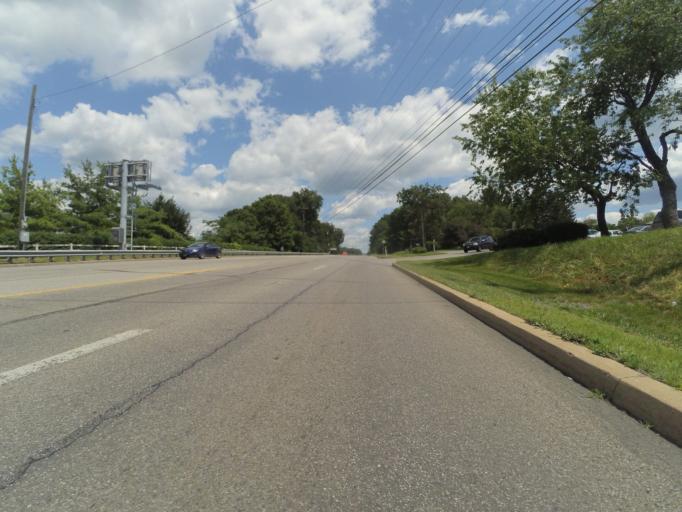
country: US
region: Pennsylvania
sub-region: Centre County
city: Lemont
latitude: 40.7844
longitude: -77.8276
